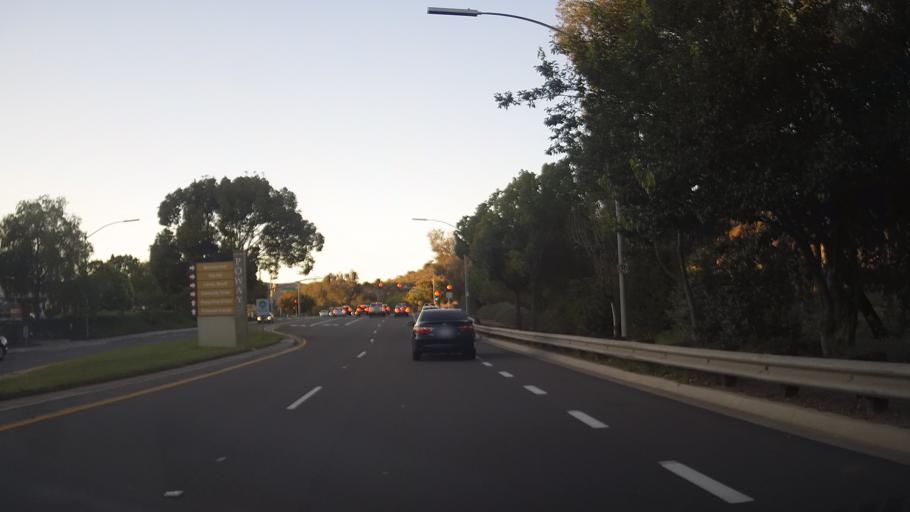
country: US
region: California
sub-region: San Diego County
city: Poway
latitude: 32.9337
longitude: -117.0596
